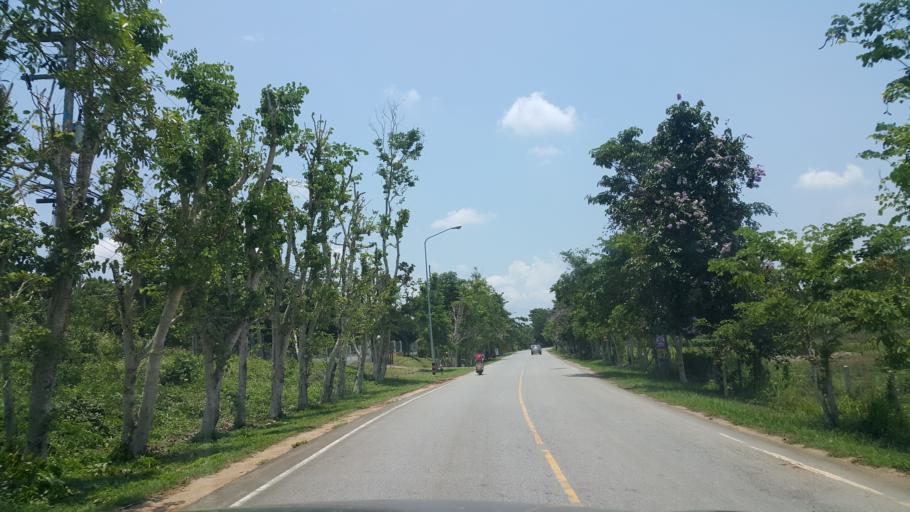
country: TH
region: Chiang Rai
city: Chiang Rai
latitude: 19.9643
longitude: 99.7752
